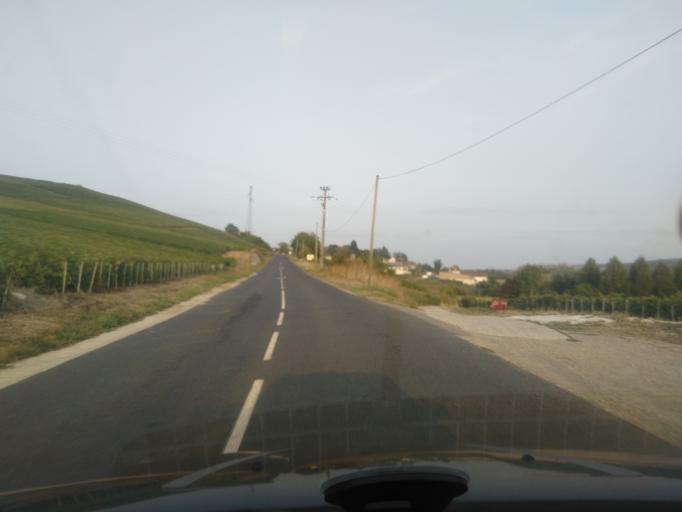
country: FR
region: Champagne-Ardenne
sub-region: Departement de la Marne
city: Mareuil-le-Port
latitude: 49.0806
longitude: 3.8076
